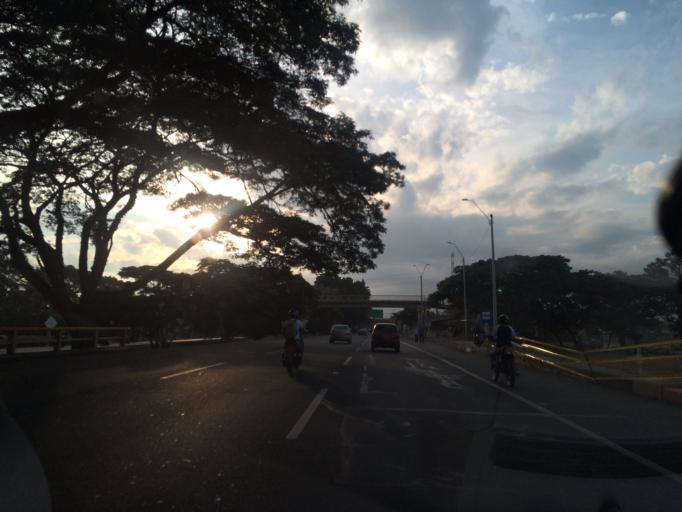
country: CO
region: Valle del Cauca
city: Cali
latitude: 3.4936
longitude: -76.4734
